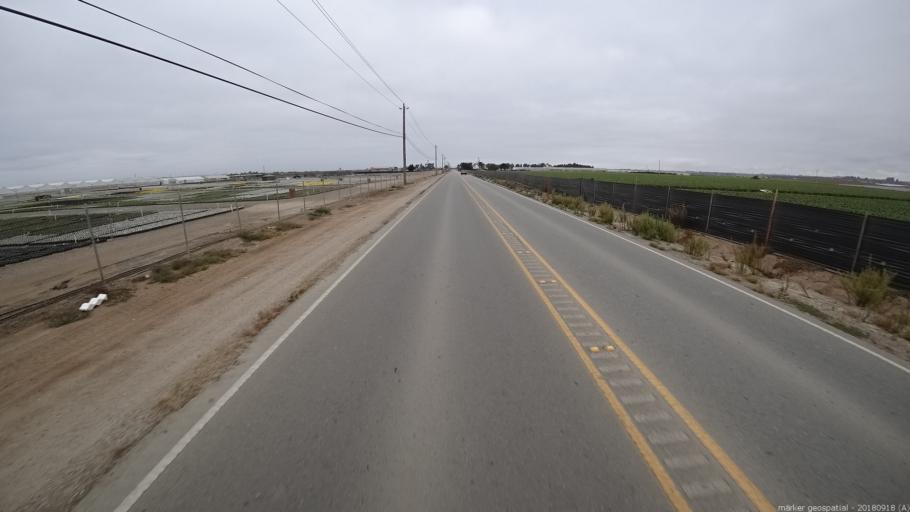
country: US
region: California
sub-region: Monterey County
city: Prunedale
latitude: 36.7407
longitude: -121.6787
